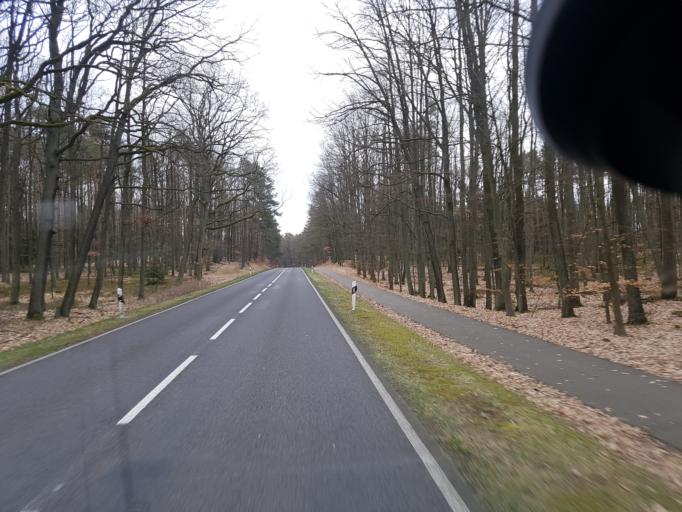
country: DE
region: Brandenburg
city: Gross Lindow
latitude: 52.1742
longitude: 14.4837
